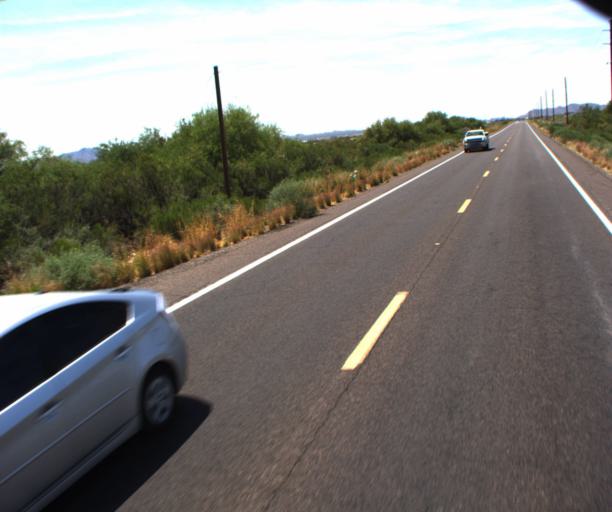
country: US
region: Arizona
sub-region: La Paz County
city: Salome
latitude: 33.8013
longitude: -113.5795
